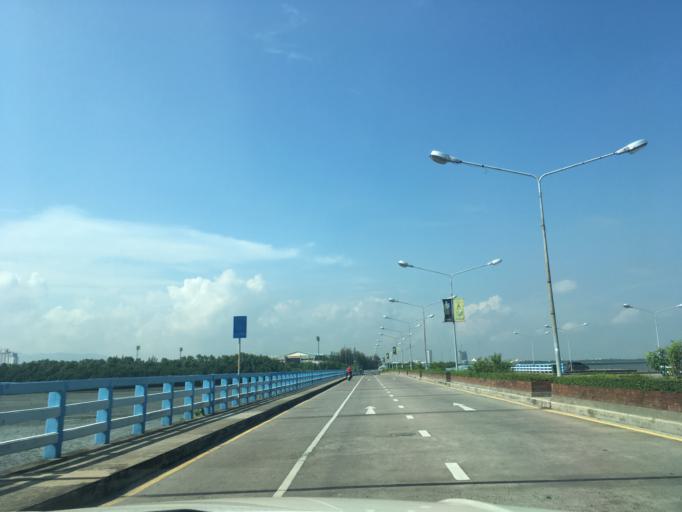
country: TH
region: Chon Buri
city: Chon Buri
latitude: 13.3695
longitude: 100.9761
